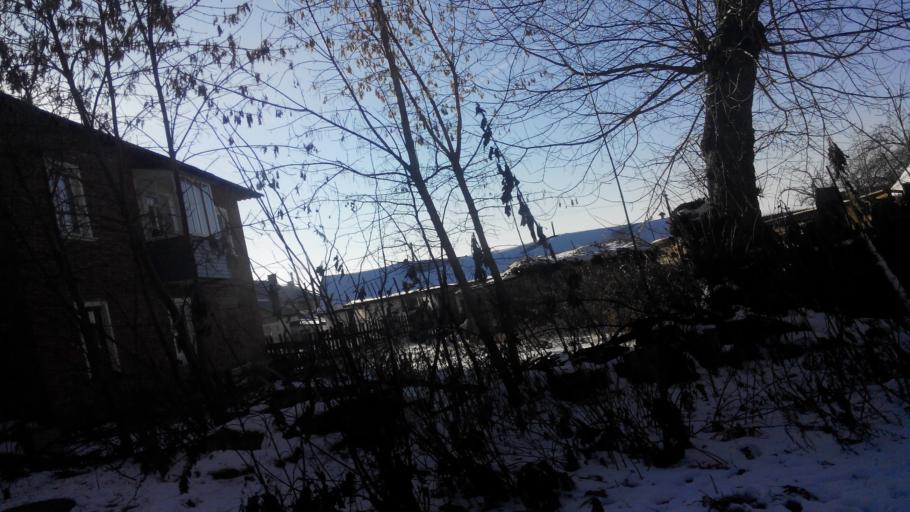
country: RU
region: Tula
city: Partizan
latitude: 53.9177
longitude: 38.0991
